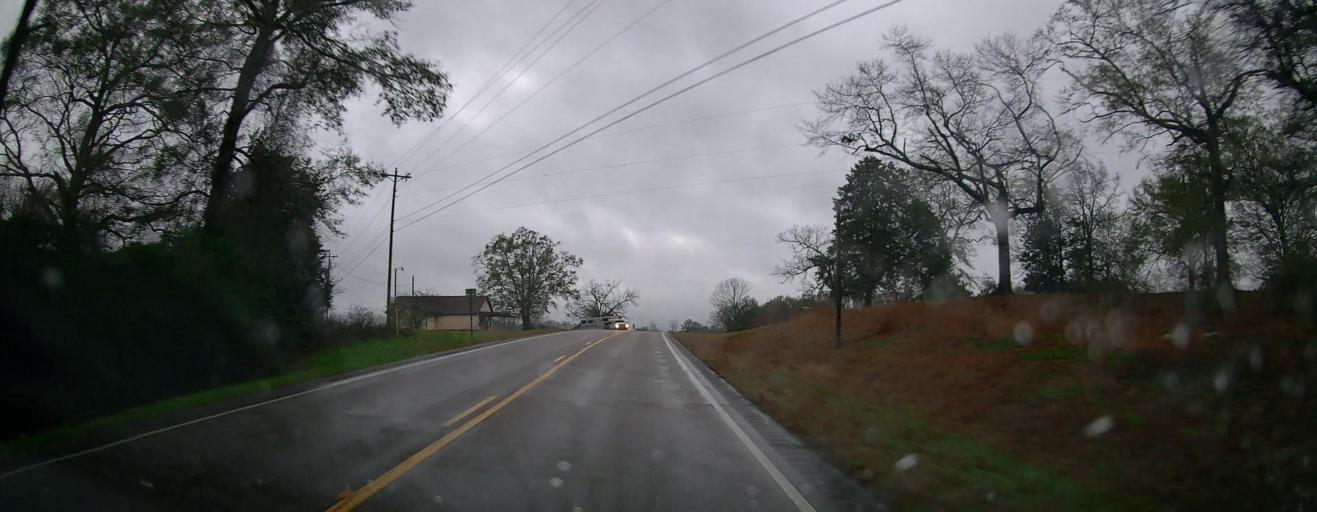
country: US
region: Alabama
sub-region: Autauga County
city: Pine Level
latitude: 32.5325
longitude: -86.6372
